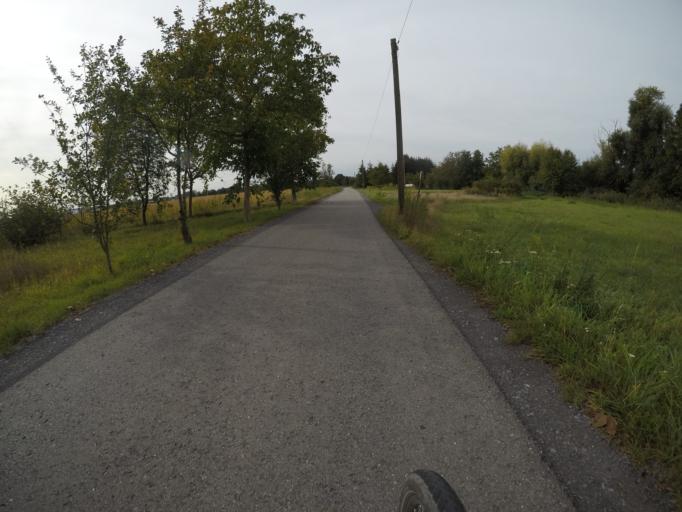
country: DE
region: Baden-Wuerttemberg
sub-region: Karlsruhe Region
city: Sankt Leon-Rot
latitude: 49.2534
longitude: 8.6306
